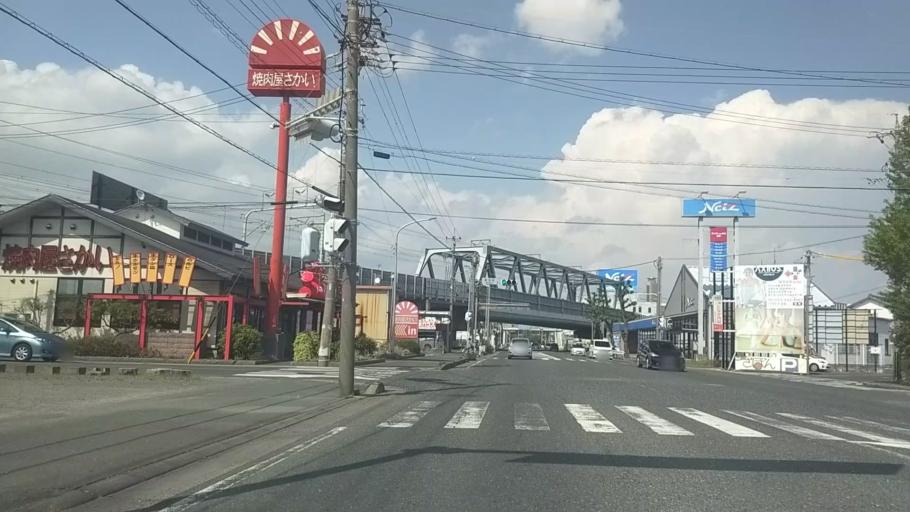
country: JP
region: Shizuoka
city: Hamamatsu
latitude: 34.6932
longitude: 137.7180
